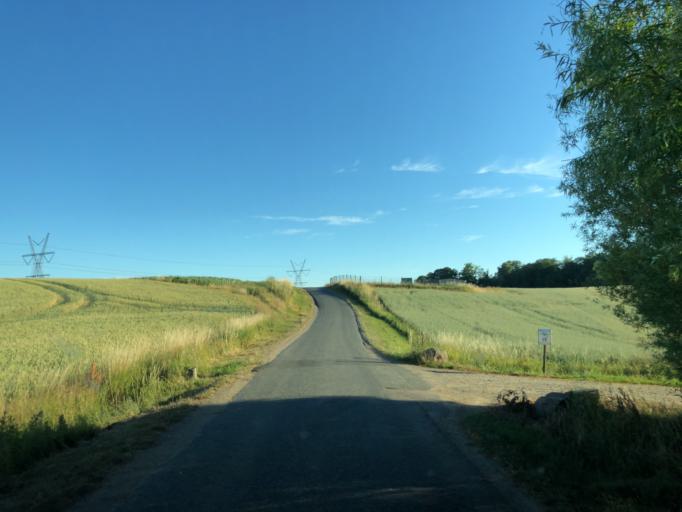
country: DK
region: Central Jutland
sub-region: Horsens Kommune
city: Horsens
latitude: 55.9147
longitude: 9.8792
